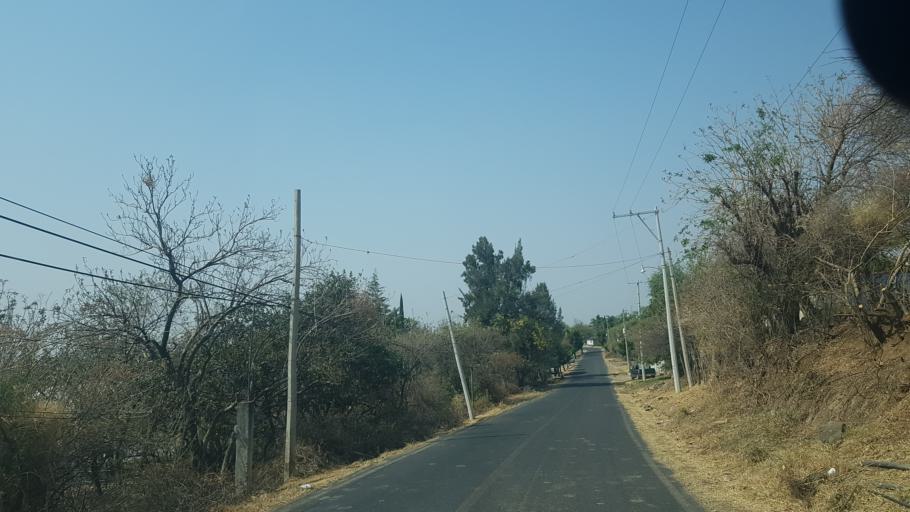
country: MX
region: Morelos
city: Tlacotepec
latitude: 18.8204
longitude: -98.7432
